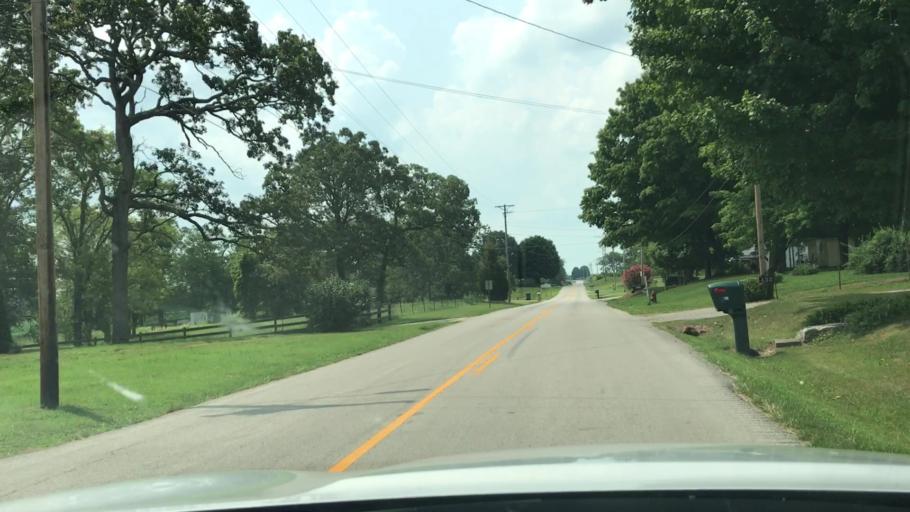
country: US
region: Kentucky
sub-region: Todd County
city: Elkton
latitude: 36.8005
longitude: -87.1488
